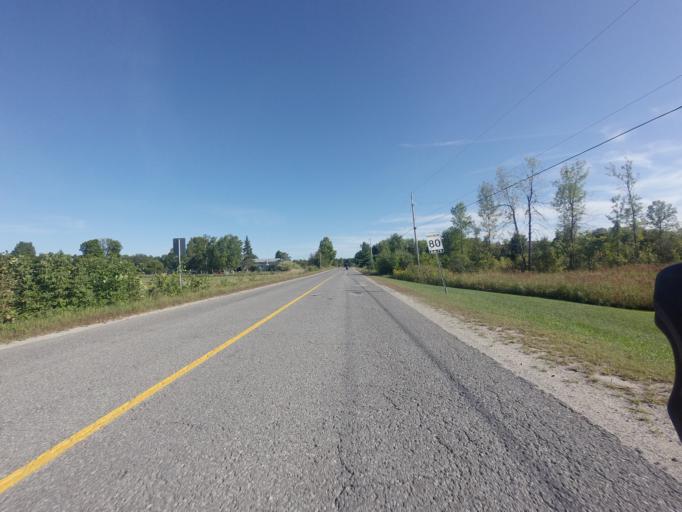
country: CA
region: Ontario
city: Perth
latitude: 44.9149
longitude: -76.3502
